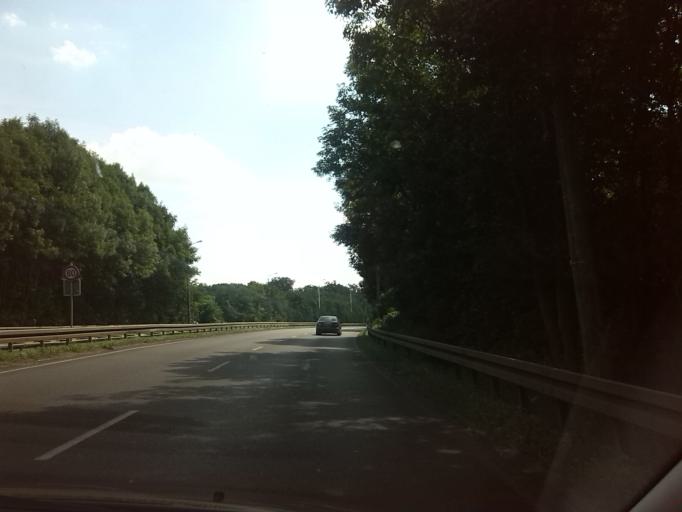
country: DE
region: Saxony
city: Markkleeberg
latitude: 51.2933
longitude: 12.3776
